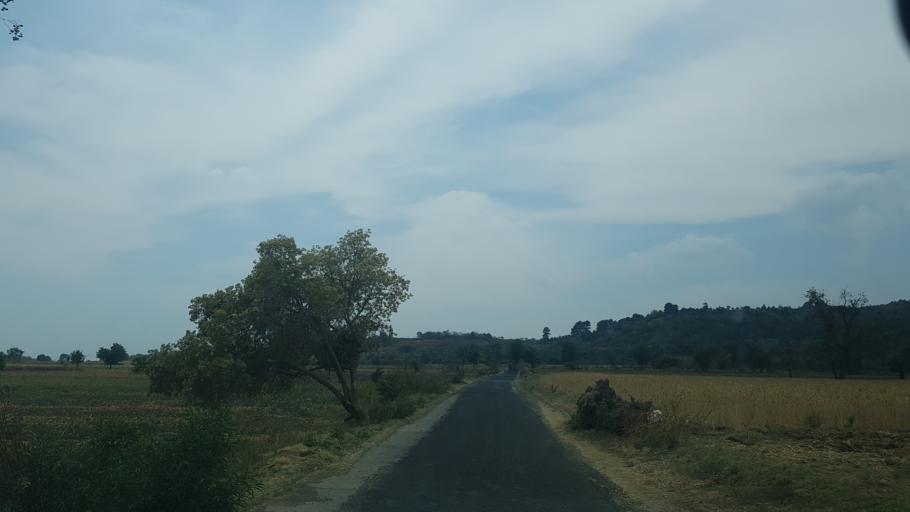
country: MX
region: Puebla
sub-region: Atzitzihuacan
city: Santiago Atzitzihuacan
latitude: 18.8576
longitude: -98.6115
